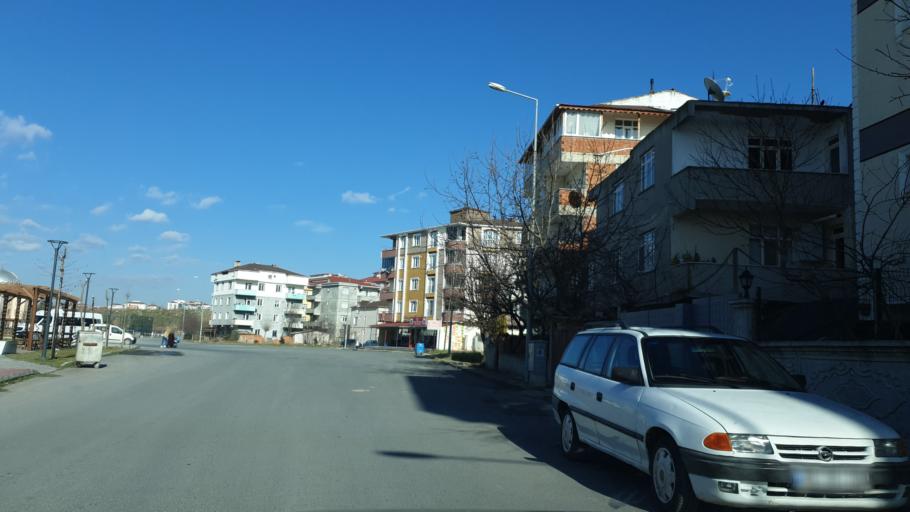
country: TR
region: Tekirdag
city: Cerkezkoey
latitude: 41.2871
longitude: 28.0064
